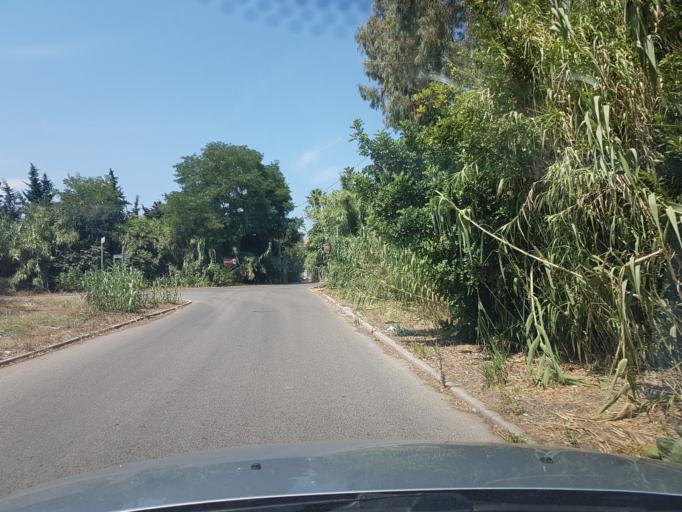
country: IT
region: Sardinia
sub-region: Provincia di Oristano
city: Donigala Fenugheddu
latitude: 39.9290
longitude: 8.5741
